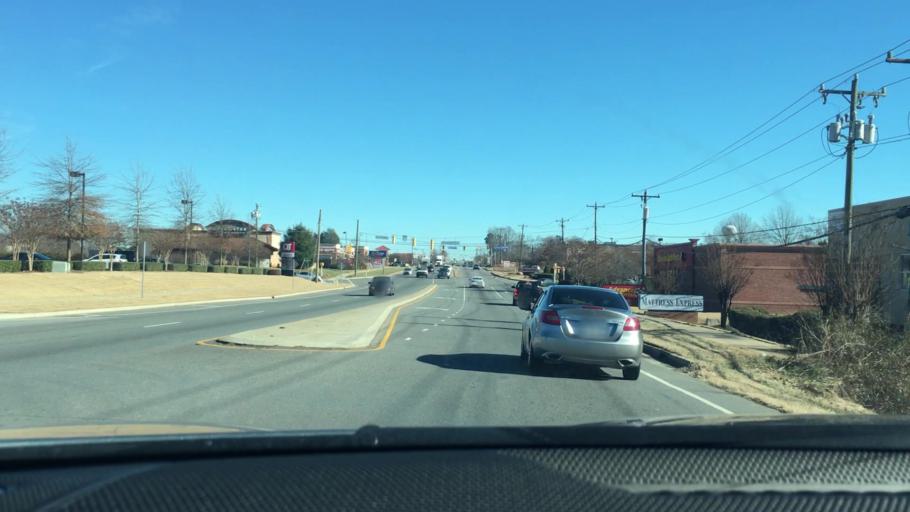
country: US
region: North Carolina
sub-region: Iredell County
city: Mooresville
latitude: 35.5963
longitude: -80.8790
